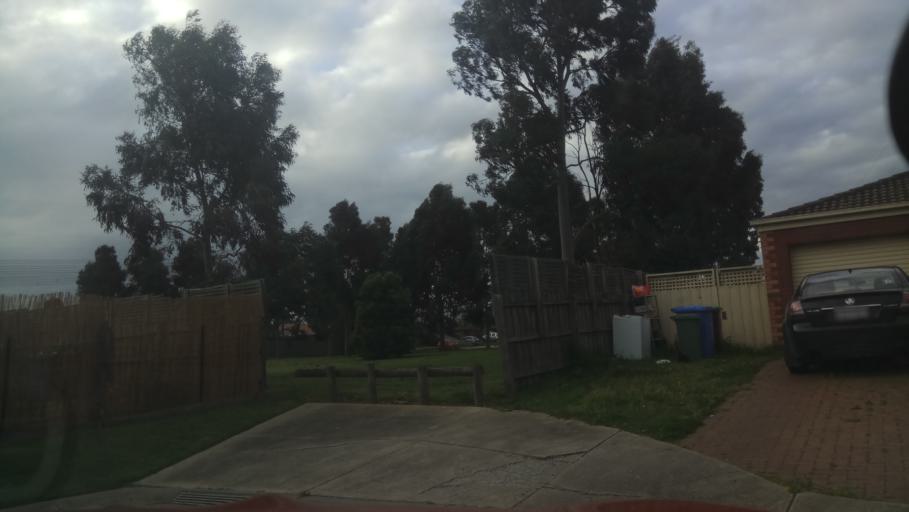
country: AU
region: Victoria
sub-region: Casey
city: Lynbrook
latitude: -38.0700
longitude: 145.2653
